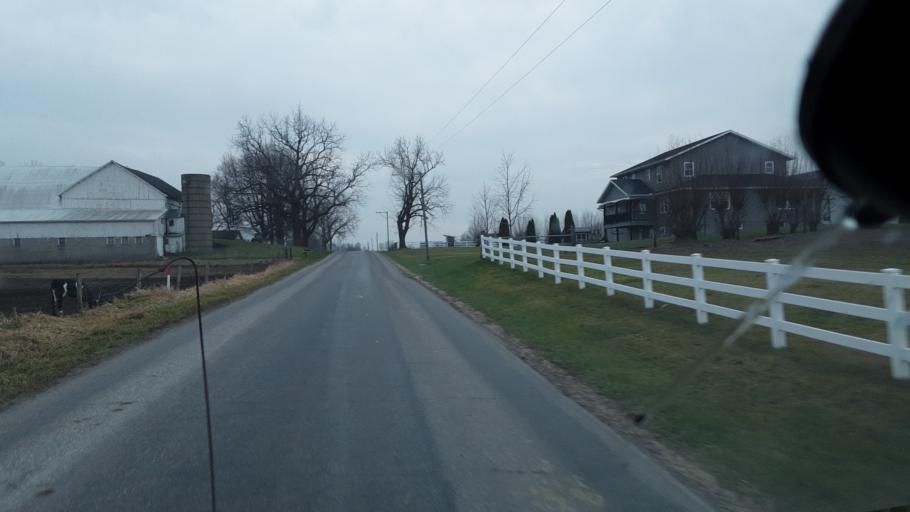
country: US
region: Indiana
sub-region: Elkhart County
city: Middlebury
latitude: 41.6844
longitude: -85.6198
